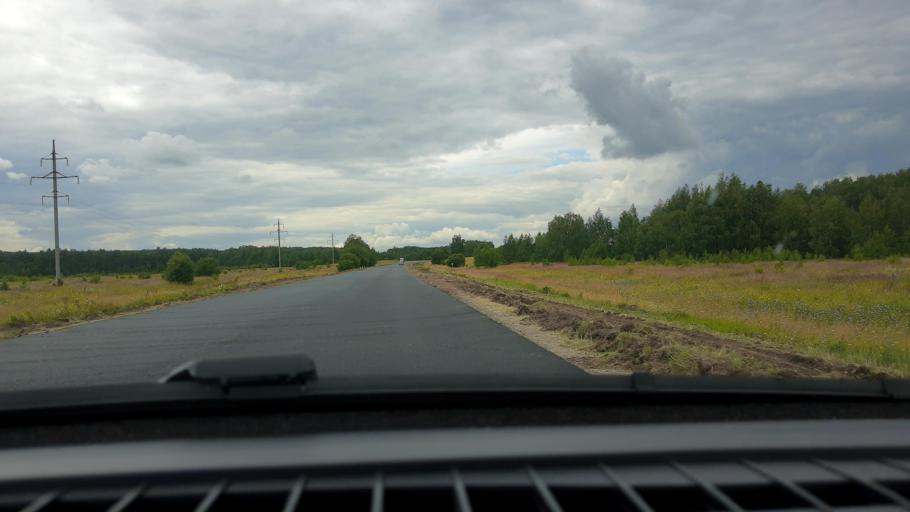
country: RU
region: Nizjnij Novgorod
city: Bol'shoye Murashkino
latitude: 55.8004
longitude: 44.8683
